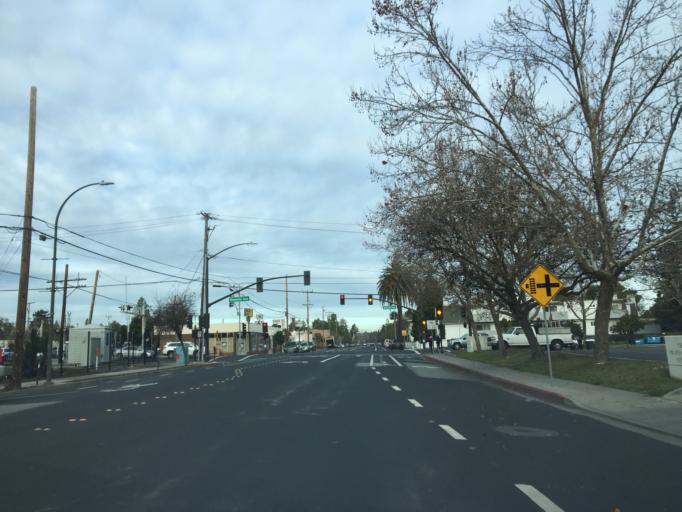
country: US
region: California
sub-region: San Mateo County
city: Redwood City
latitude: 37.4877
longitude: -122.2341
